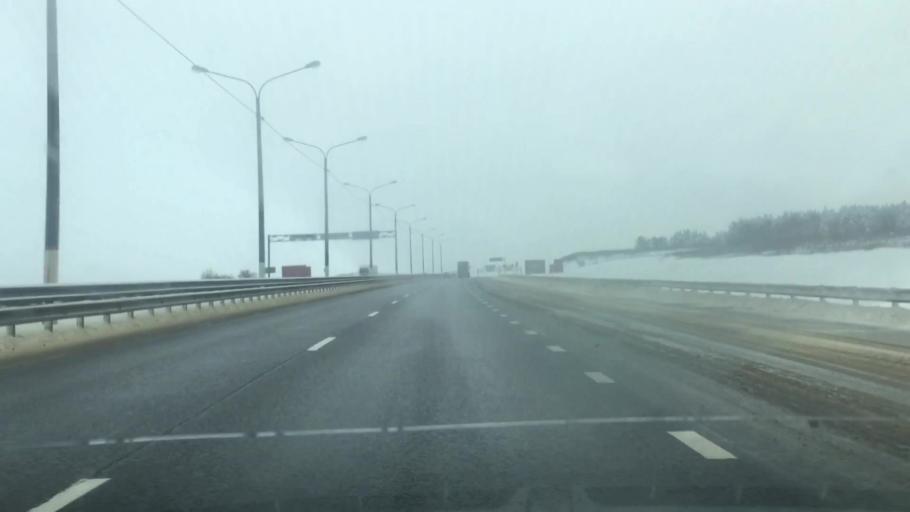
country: RU
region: Tula
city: Yefremov
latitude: 53.1600
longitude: 38.2494
